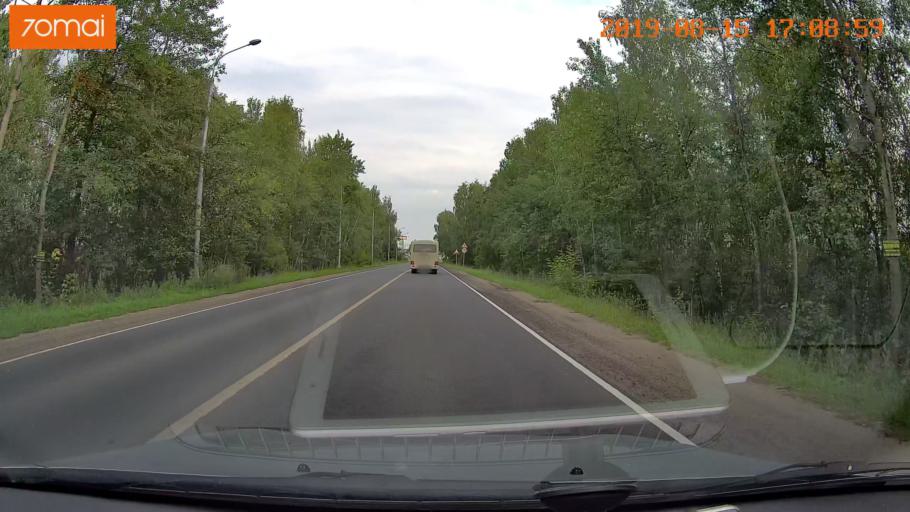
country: RU
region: Moskovskaya
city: Beloozerskiy
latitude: 55.4538
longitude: 38.4329
